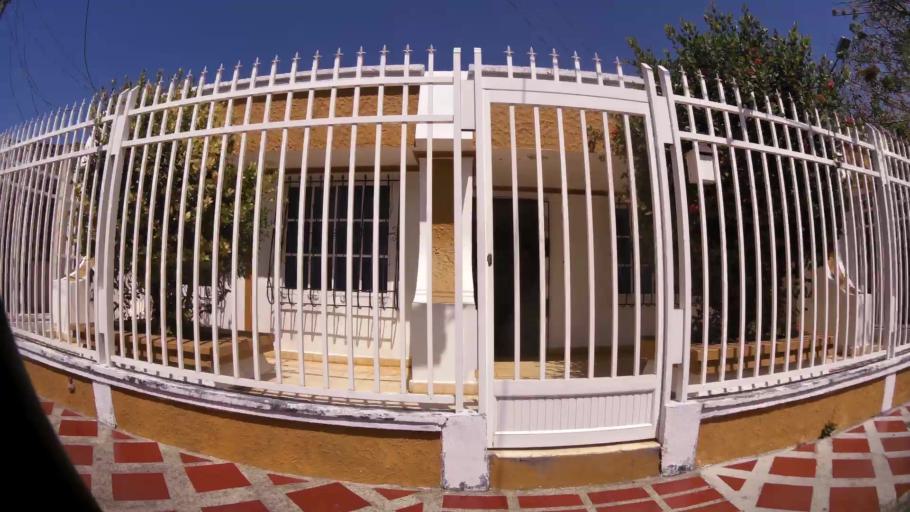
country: CO
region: Atlantico
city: Barranquilla
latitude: 10.9791
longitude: -74.8192
